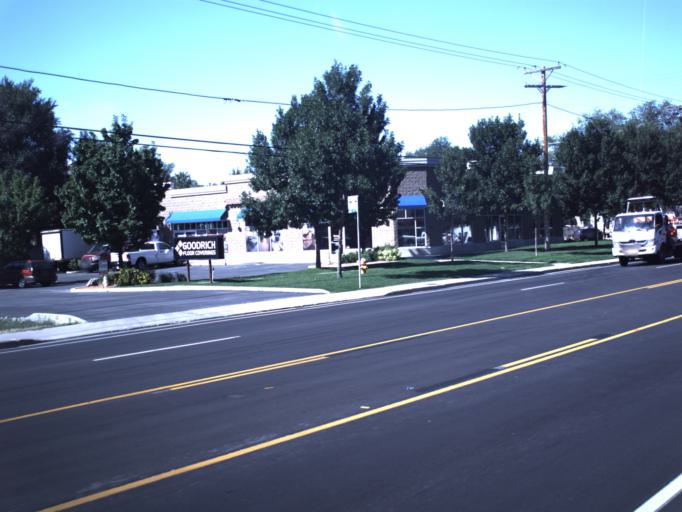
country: US
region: Utah
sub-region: Salt Lake County
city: Millcreek
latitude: 40.6744
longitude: -111.8677
